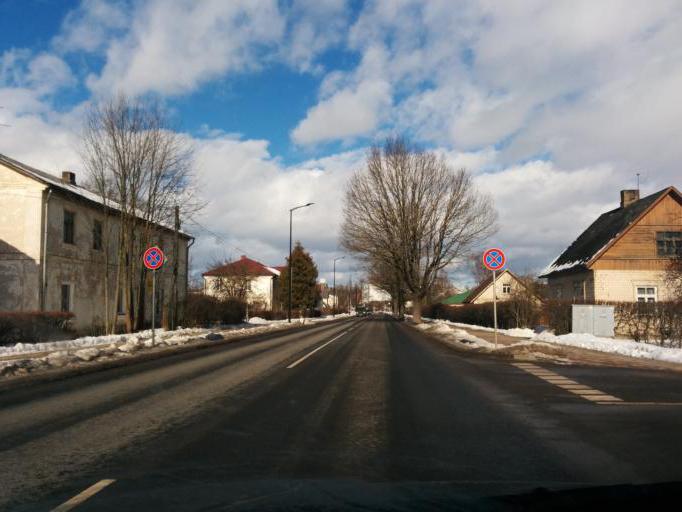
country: LV
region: Gulbenes Rajons
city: Gulbene
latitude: 57.1662
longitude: 26.7563
